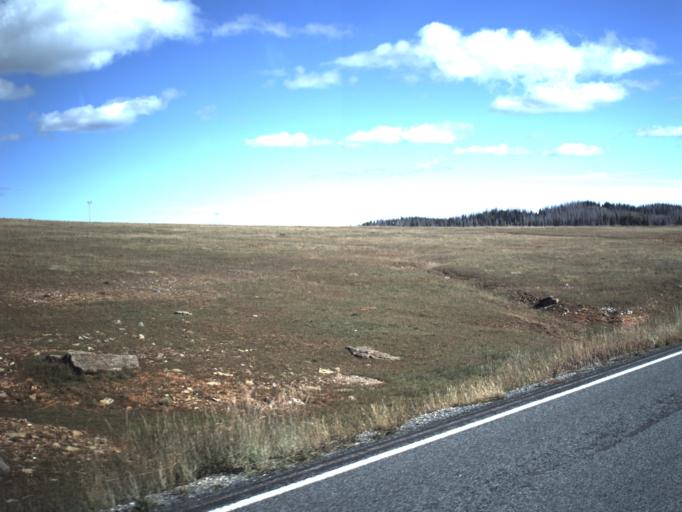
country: US
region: Utah
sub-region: Iron County
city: Parowan
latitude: 37.6712
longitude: -112.8406
